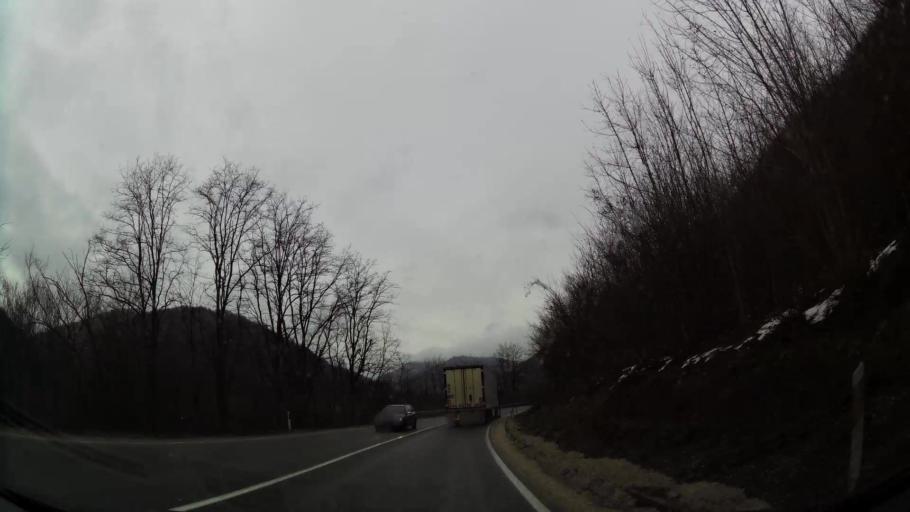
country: RS
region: Central Serbia
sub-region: Pcinjski Okrug
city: Vladicin Han
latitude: 42.7401
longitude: 22.0600
